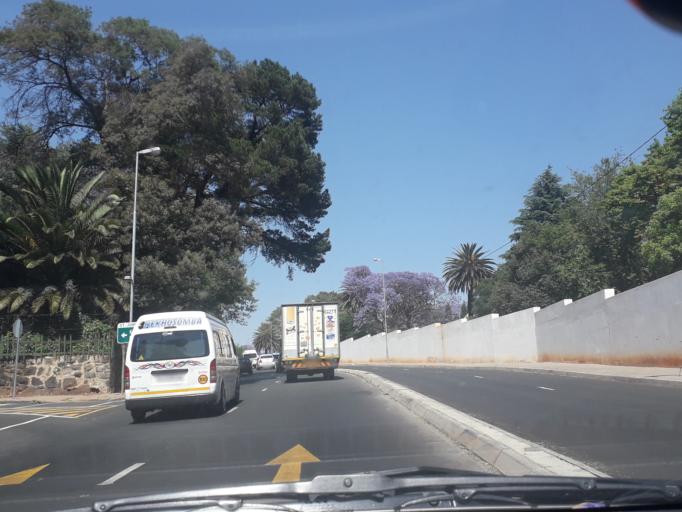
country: ZA
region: Gauteng
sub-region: City of Johannesburg Metropolitan Municipality
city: Johannesburg
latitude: -26.1727
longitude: 28.0697
